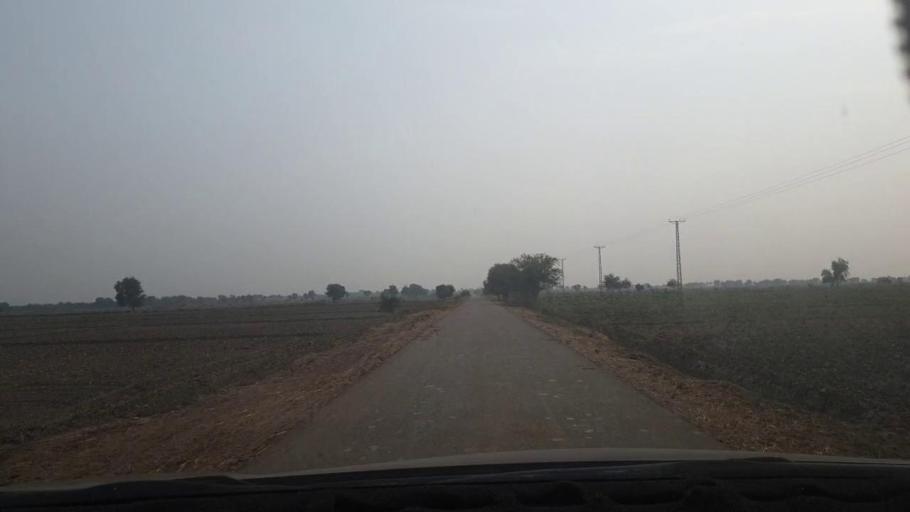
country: PK
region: Sindh
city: Jamshoro
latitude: 25.5200
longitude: 68.3145
